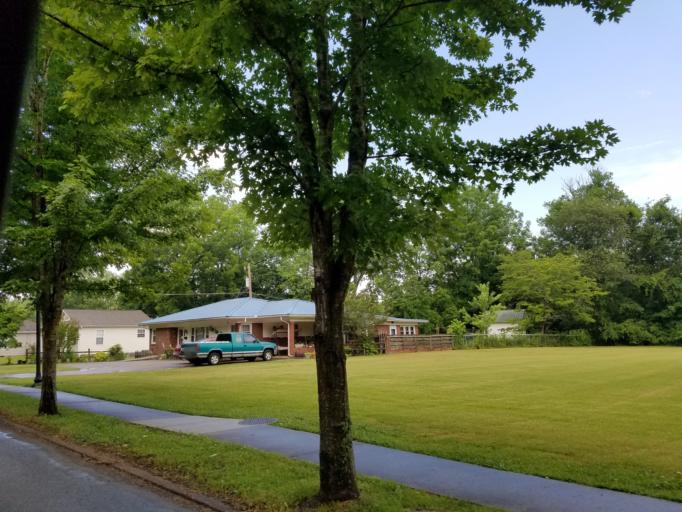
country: US
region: Tennessee
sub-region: Humphreys County
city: Waverly
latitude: 36.0825
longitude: -87.7828
